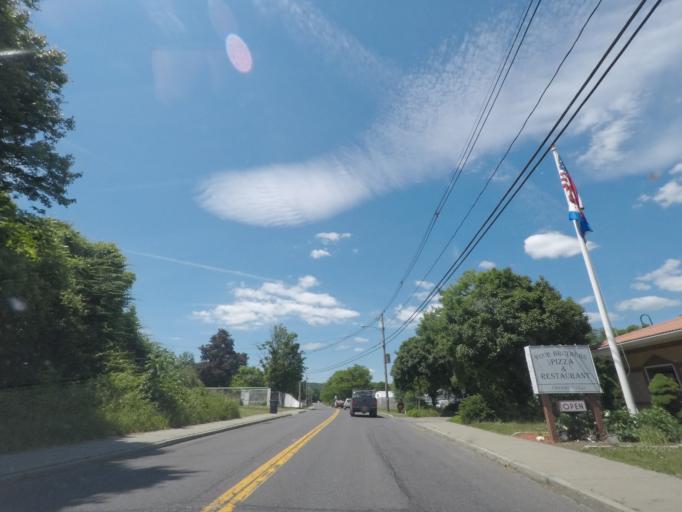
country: US
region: New York
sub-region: Dutchess County
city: Pine Plains
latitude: 41.9555
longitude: -73.5148
